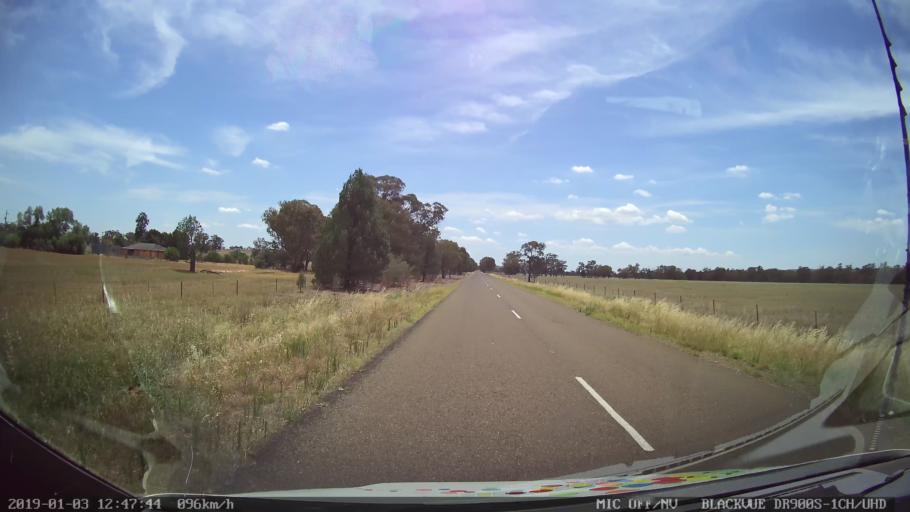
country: AU
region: New South Wales
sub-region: Weddin
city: Grenfell
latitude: -33.7231
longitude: 148.2445
